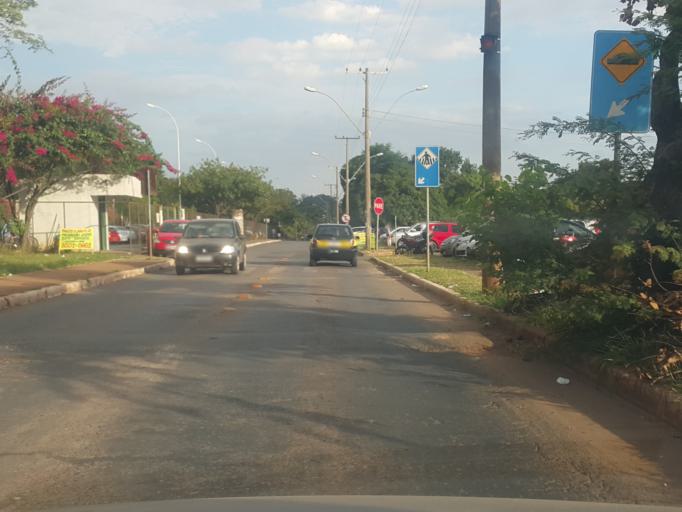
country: BR
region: Federal District
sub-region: Brasilia
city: Brasilia
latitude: -15.8223
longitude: -48.0705
